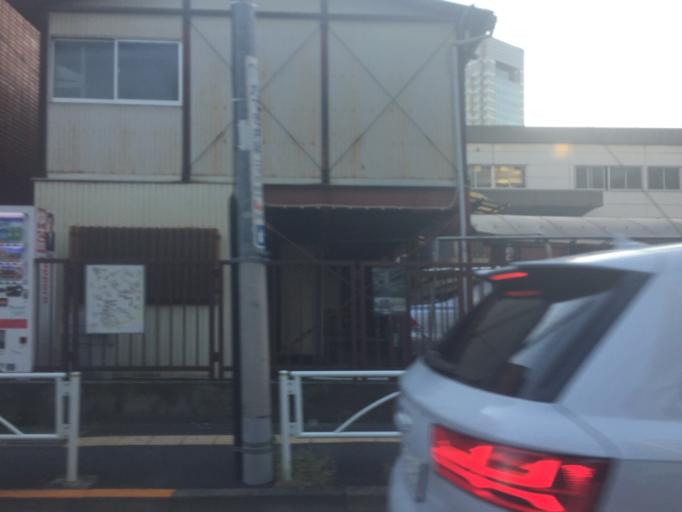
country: JP
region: Tokyo
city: Tokyo
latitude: 35.6271
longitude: 139.6360
